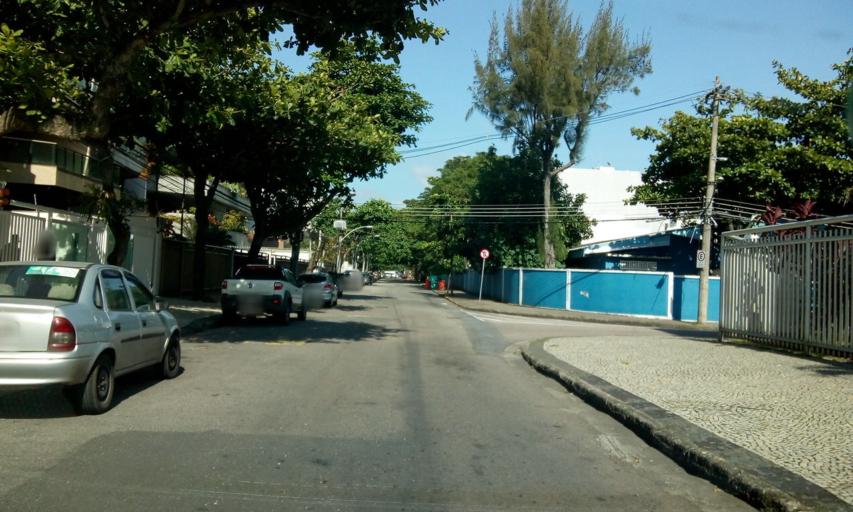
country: BR
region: Rio de Janeiro
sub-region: Rio De Janeiro
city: Rio de Janeiro
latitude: -23.0134
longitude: -43.3021
